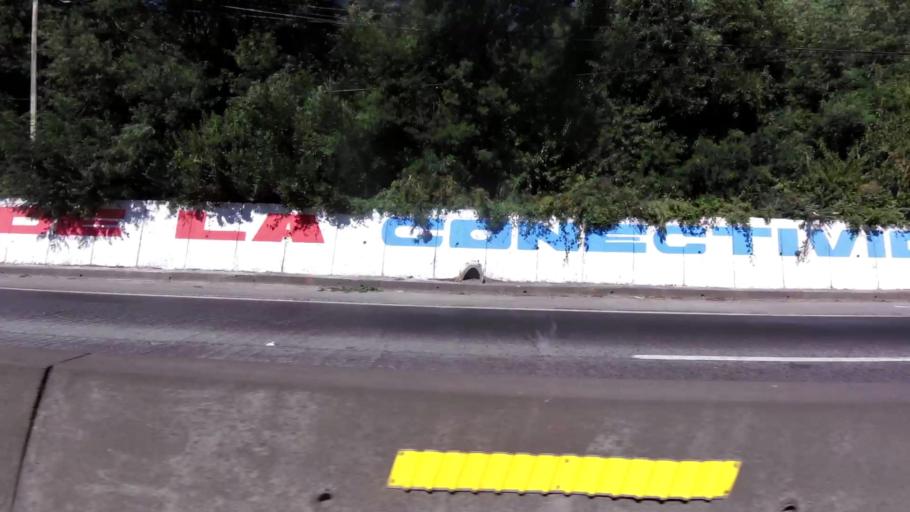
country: CL
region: Biobio
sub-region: Provincia de Concepcion
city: Concepcion
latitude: -36.8018
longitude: -73.0257
